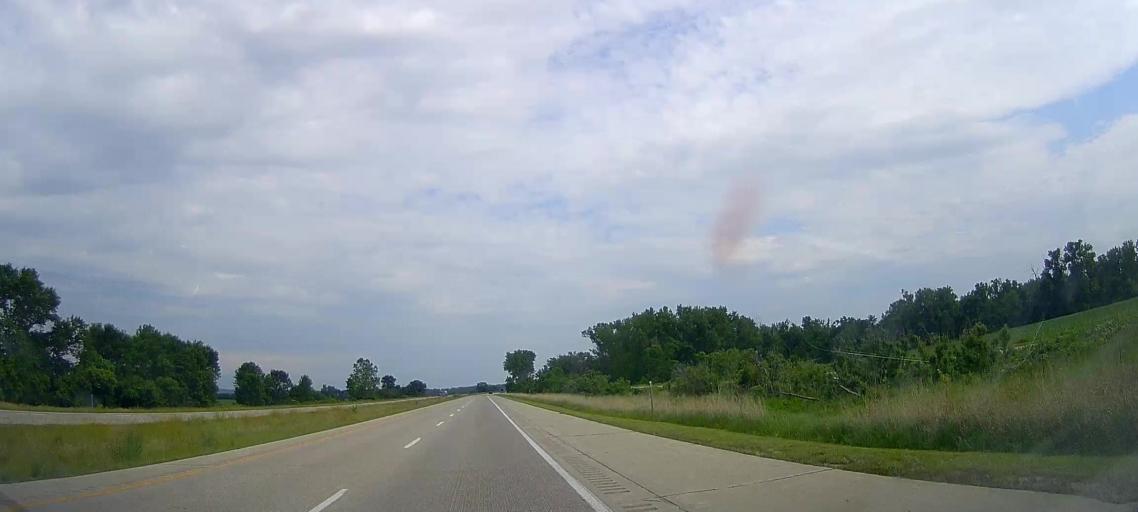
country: US
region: Nebraska
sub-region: Burt County
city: Tekamah
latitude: 41.8417
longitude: -96.0903
